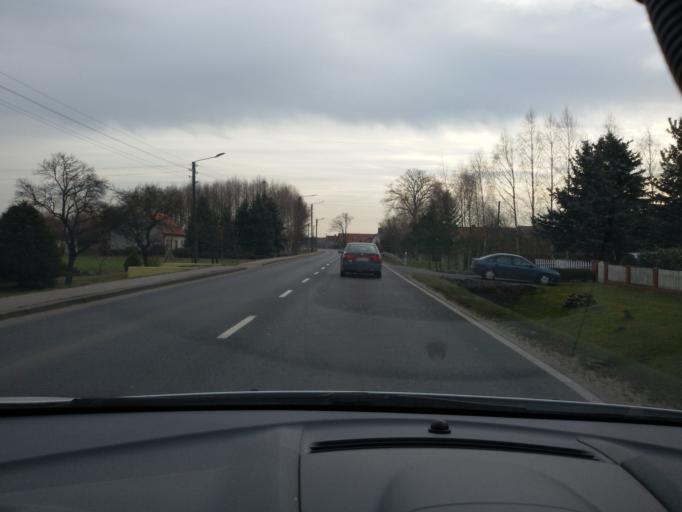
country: PL
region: Lubusz
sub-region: Powiat wschowski
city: Wschowa
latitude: 51.8172
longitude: 16.3820
